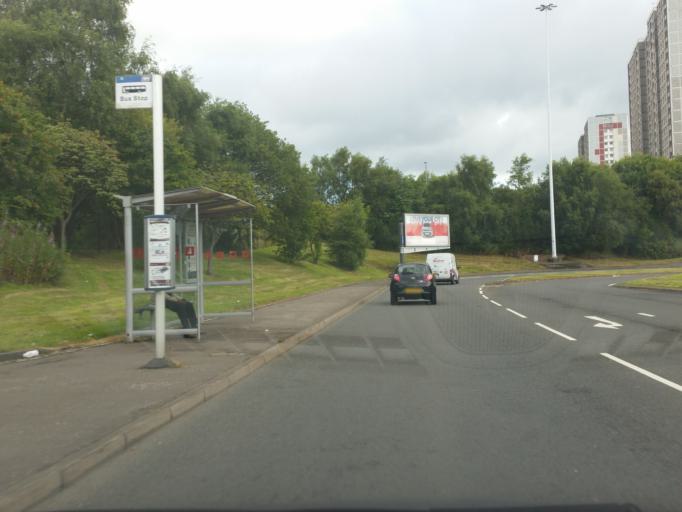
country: GB
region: Scotland
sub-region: Glasgow City
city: Glasgow
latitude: 55.8693
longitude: -4.2361
